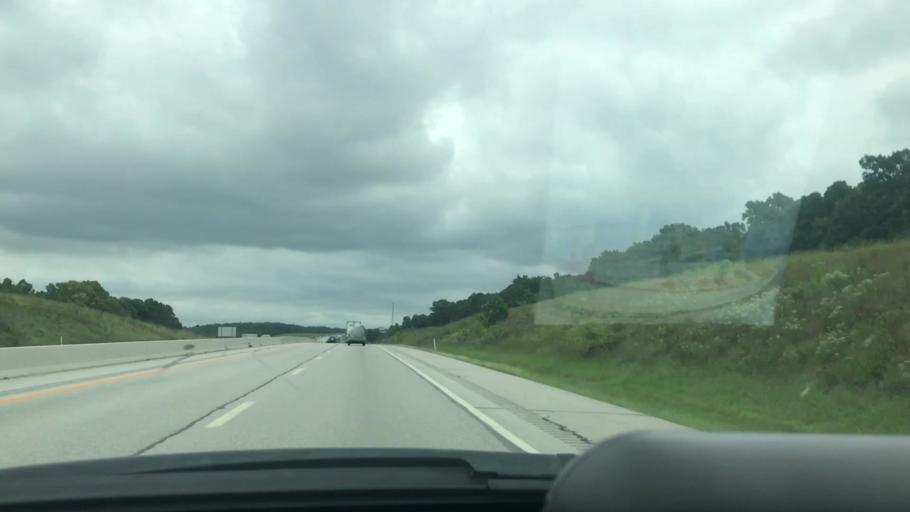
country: US
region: Kansas
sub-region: Cherokee County
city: Galena
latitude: 36.9801
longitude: -94.6376
